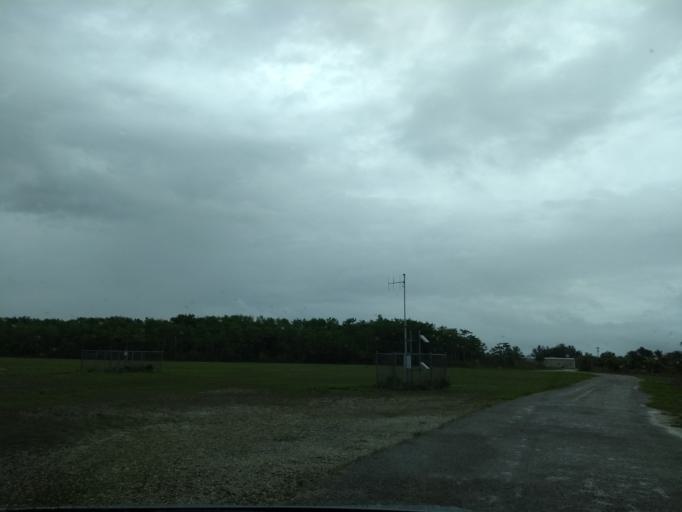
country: US
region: Florida
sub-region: Collier County
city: Lely Resort
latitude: 25.9525
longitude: -81.3640
